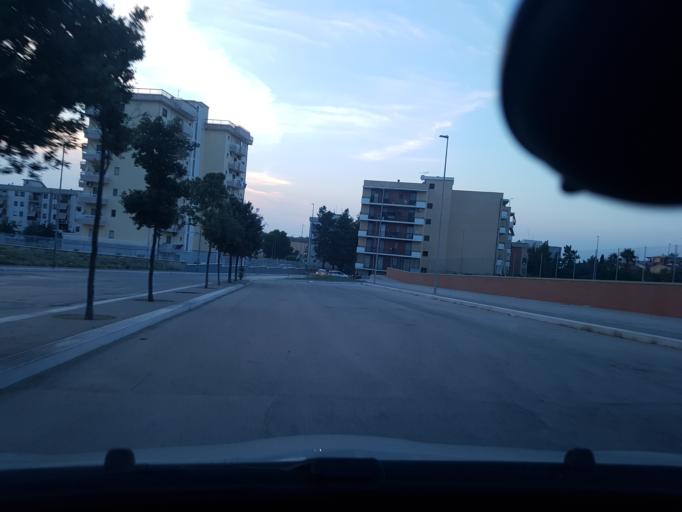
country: IT
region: Apulia
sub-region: Provincia di Foggia
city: Cerignola
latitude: 41.2595
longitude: 15.8762
